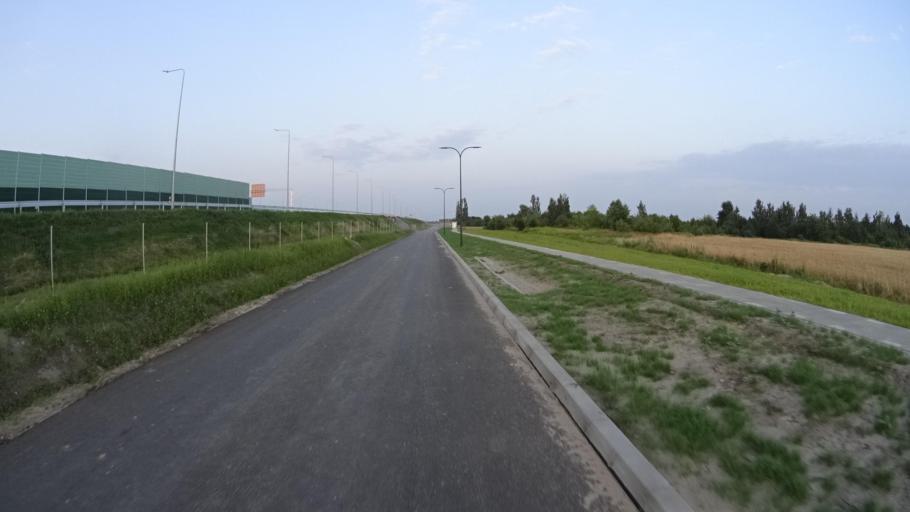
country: PL
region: Masovian Voivodeship
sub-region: Warszawa
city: Wilanow
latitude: 52.1522
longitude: 21.0814
